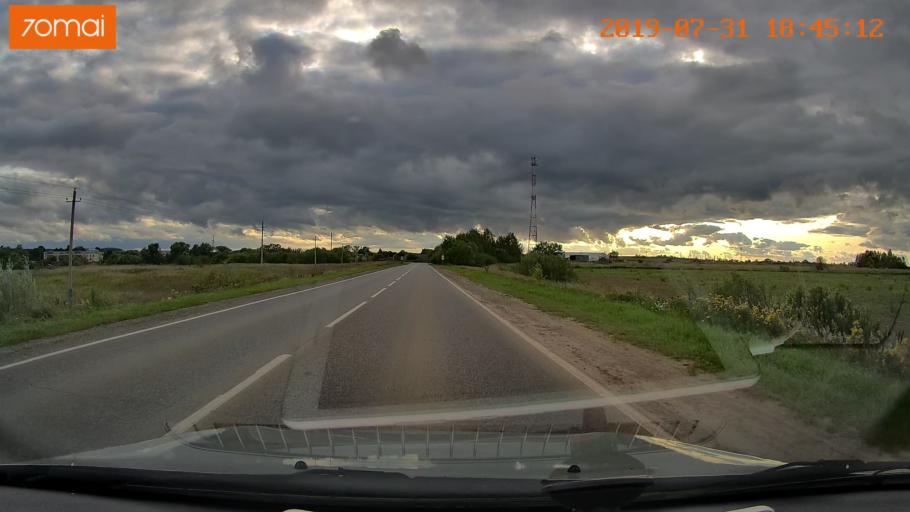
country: RU
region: Moskovskaya
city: Troitskoye
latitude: 55.2519
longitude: 38.5363
